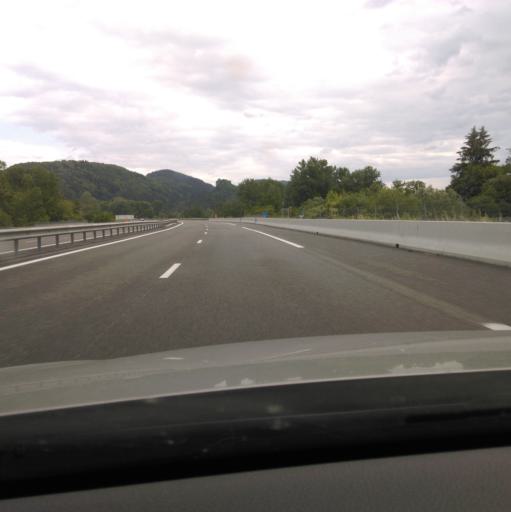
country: FR
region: Rhone-Alpes
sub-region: Departement de l'Ain
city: Montreal-la-Cluse
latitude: 46.1677
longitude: 5.5602
